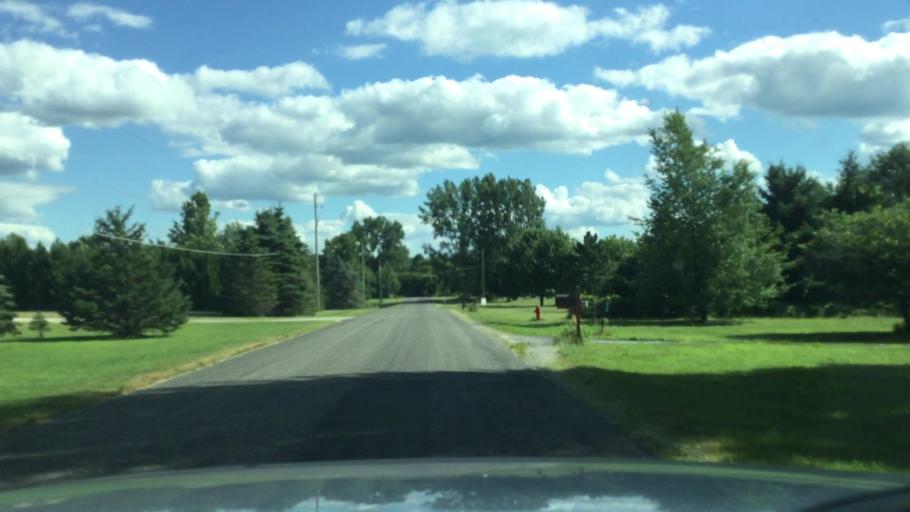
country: US
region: Michigan
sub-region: Saginaw County
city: Saint Charles
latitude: 43.3682
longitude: -84.1607
